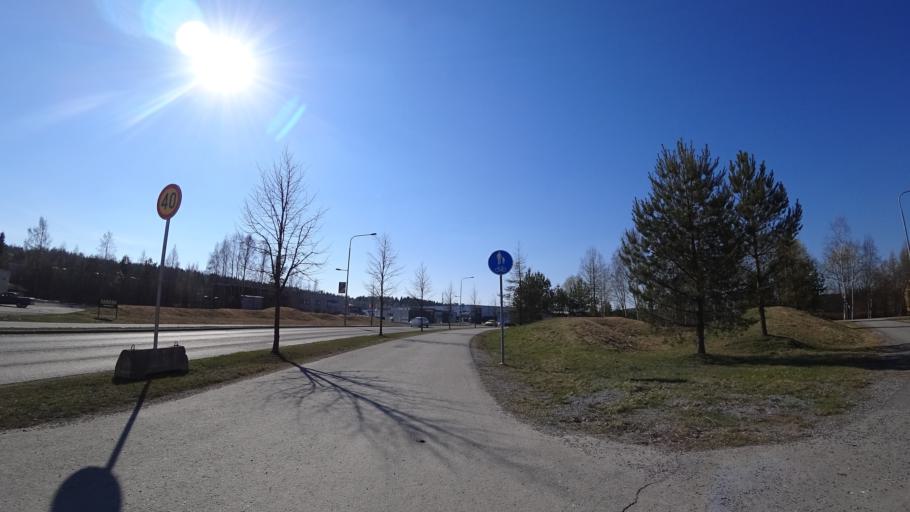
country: FI
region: Pirkanmaa
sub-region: Tampere
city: Pirkkala
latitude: 61.5187
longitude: 23.6625
